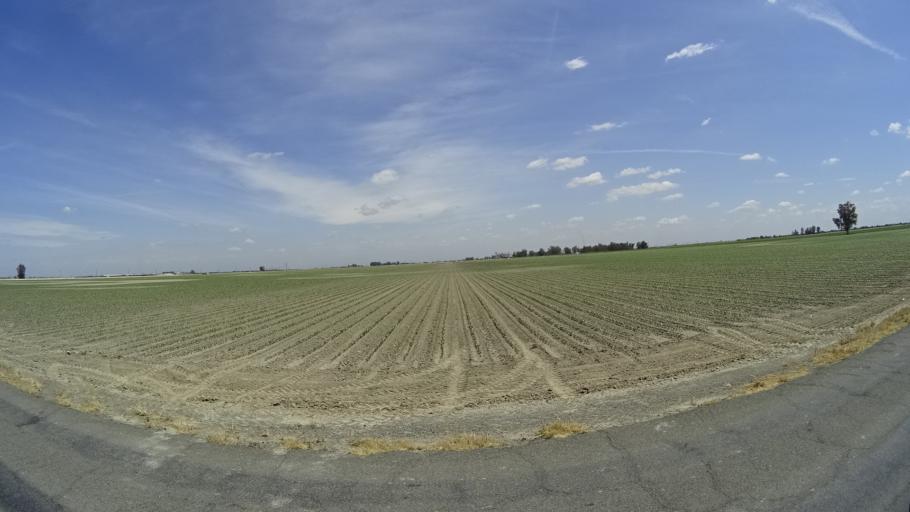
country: US
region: California
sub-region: Kings County
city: Home Garden
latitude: 36.2205
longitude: -119.6728
